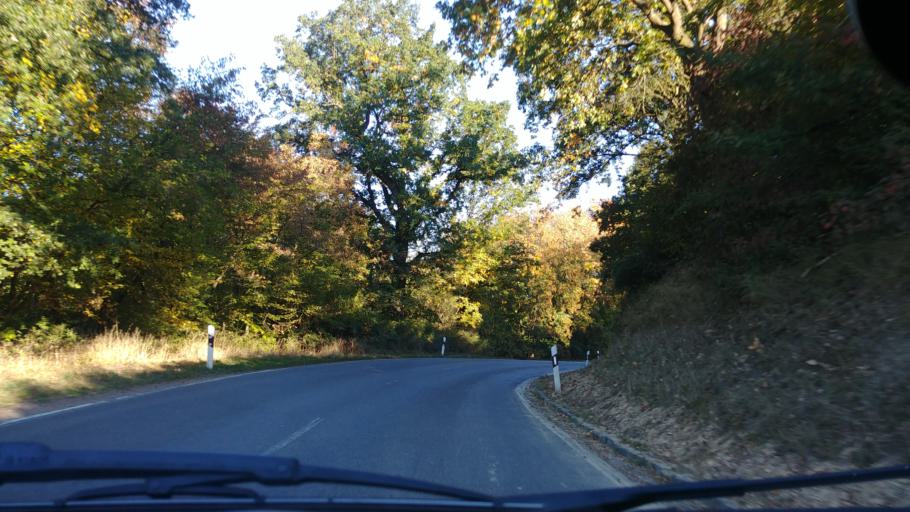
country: DE
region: Rheinland-Pfalz
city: Miehlen
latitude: 50.2205
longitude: 7.8340
